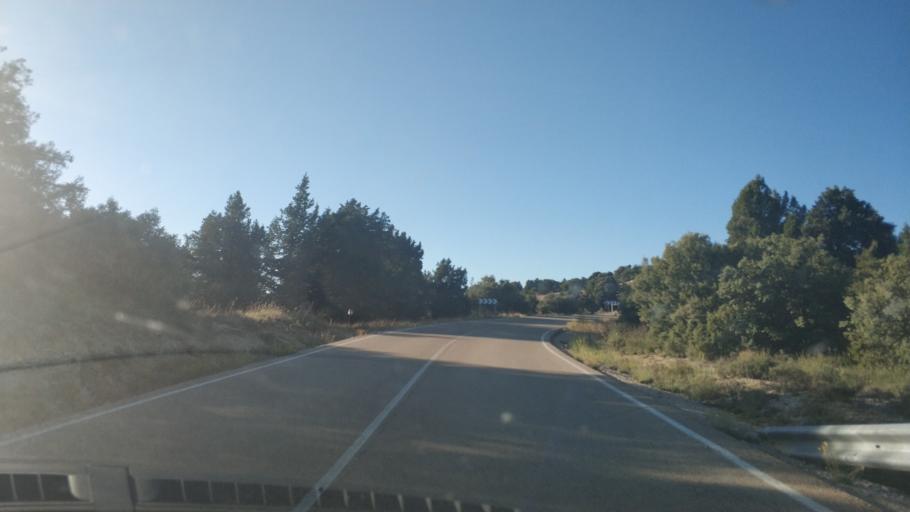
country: ES
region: Castille and Leon
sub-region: Provincia de Soria
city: Liceras
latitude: 41.4454
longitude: -3.2166
